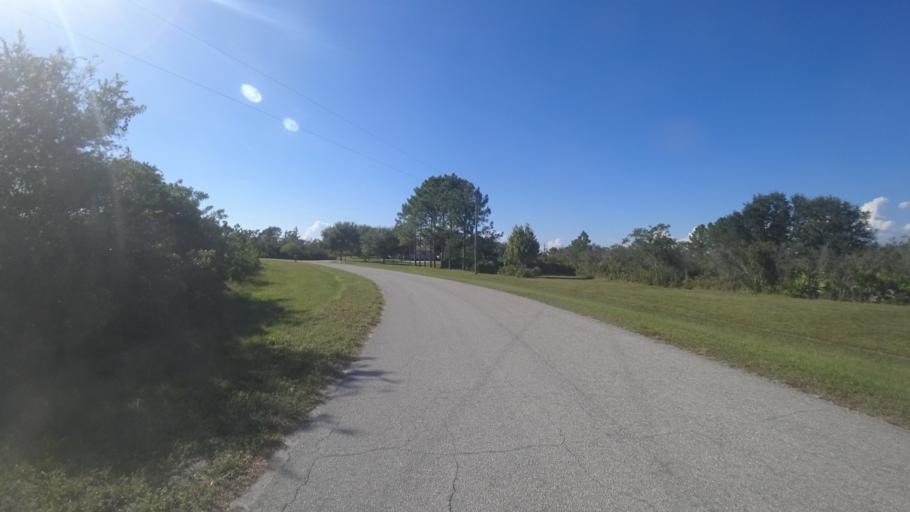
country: US
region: Florida
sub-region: Sarasota County
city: The Meadows
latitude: 27.4167
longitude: -82.2809
